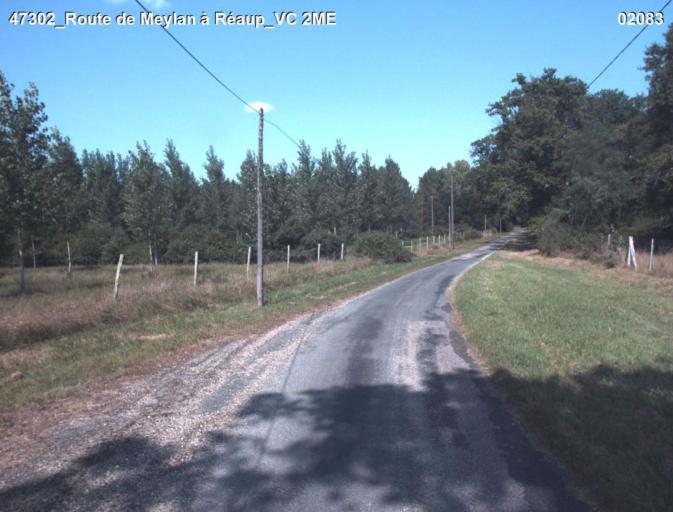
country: FR
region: Aquitaine
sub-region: Departement du Lot-et-Garonne
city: Mezin
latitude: 44.0913
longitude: 0.1285
